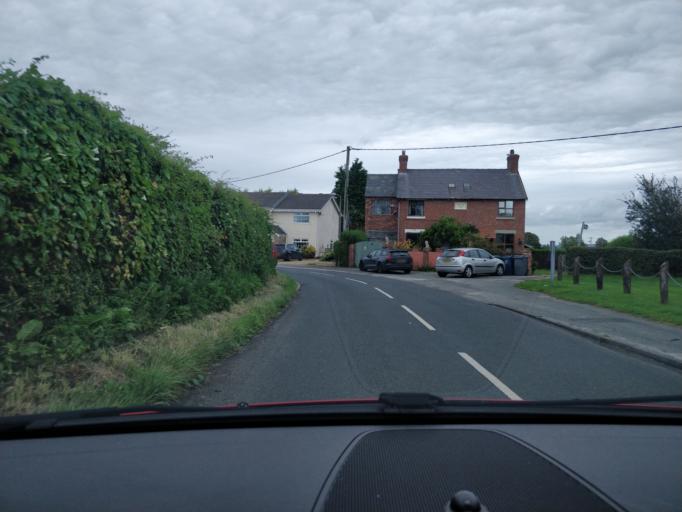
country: GB
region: England
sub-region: Lancashire
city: Ormskirk
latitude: 53.6045
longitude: -2.8651
